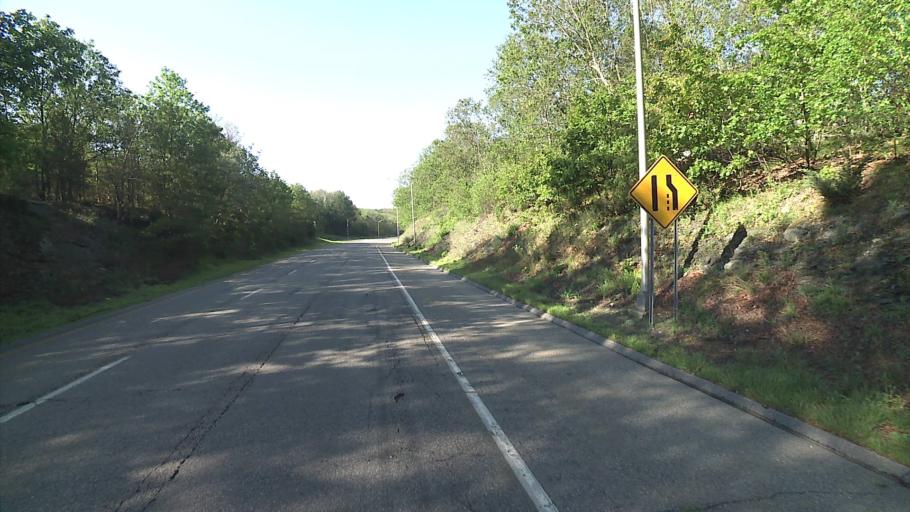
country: US
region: Connecticut
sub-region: Windham County
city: Wauregan
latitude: 41.7617
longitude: -71.8739
